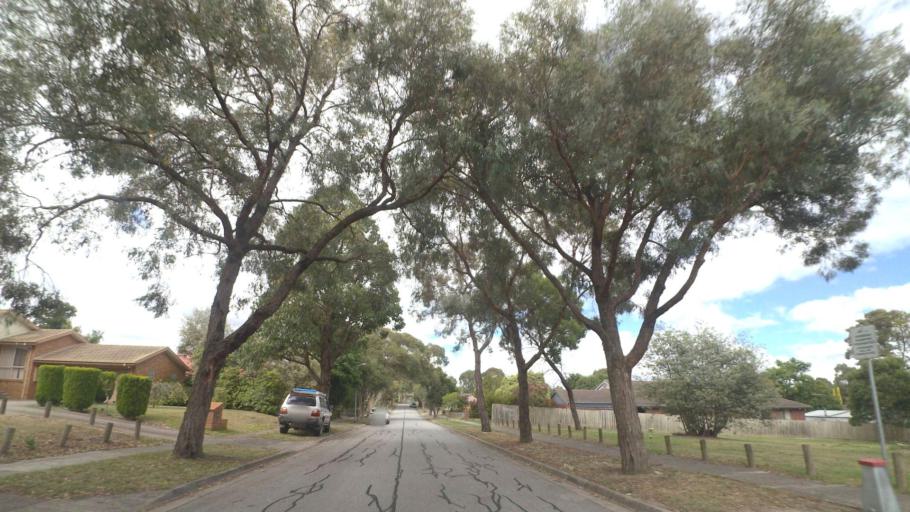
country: AU
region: Victoria
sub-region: Maroondah
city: Bayswater North
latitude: -37.8305
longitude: 145.3070
